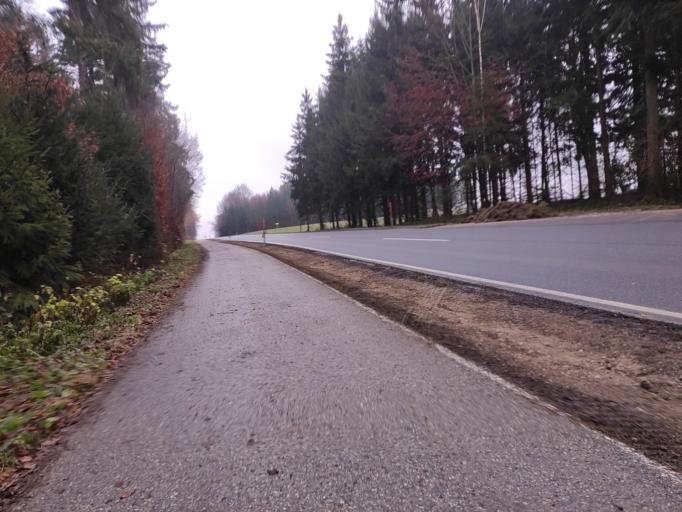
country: AT
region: Salzburg
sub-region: Politischer Bezirk Salzburg-Umgebung
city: Seekirchen am Wallersee
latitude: 47.9094
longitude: 13.1144
